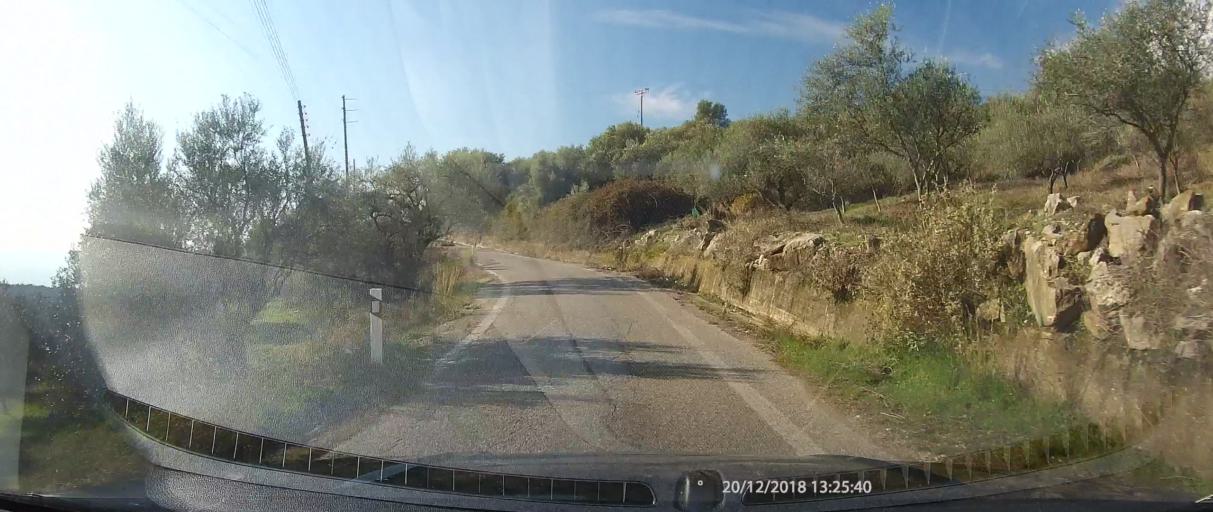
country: GR
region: West Greece
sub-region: Nomos Aitolias kai Akarnanias
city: Paravola
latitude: 38.6252
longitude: 21.5667
